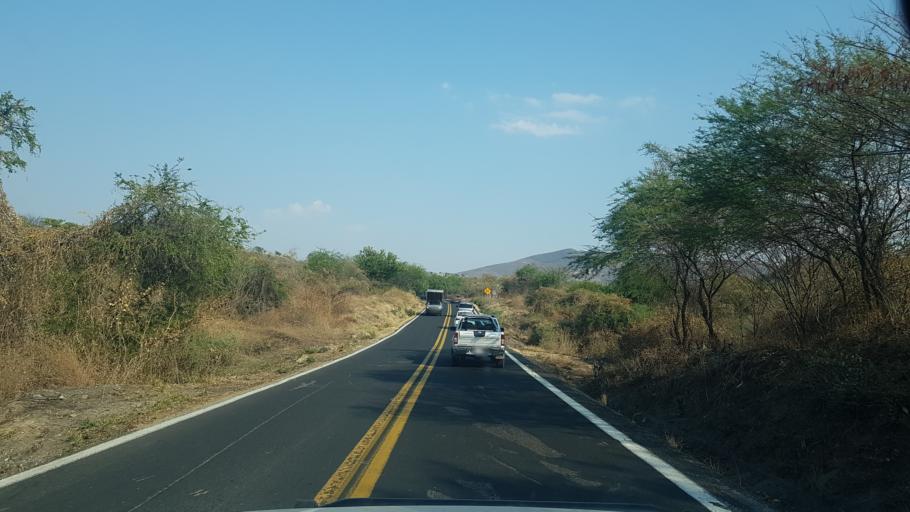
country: MX
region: Puebla
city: Calmeca
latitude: 18.6454
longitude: -98.6444
